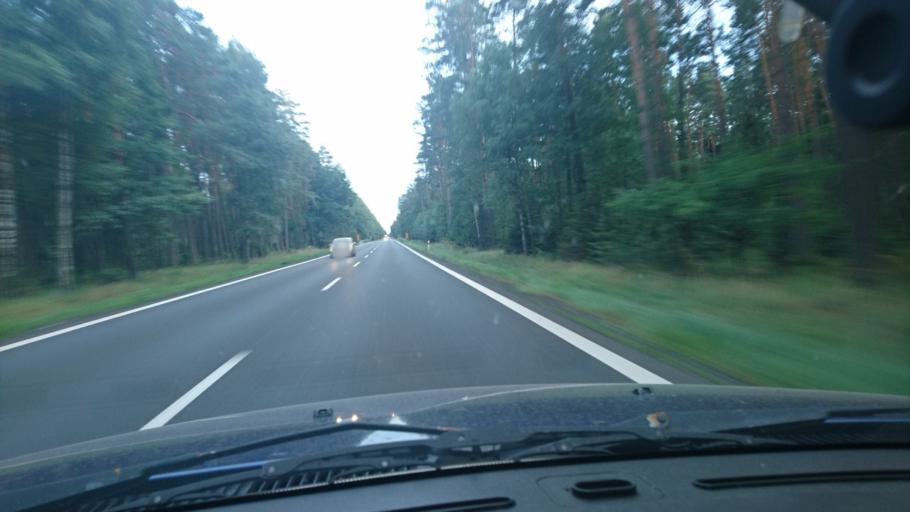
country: PL
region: Silesian Voivodeship
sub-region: Powiat tarnogorski
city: Tworog
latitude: 50.5751
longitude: 18.7096
